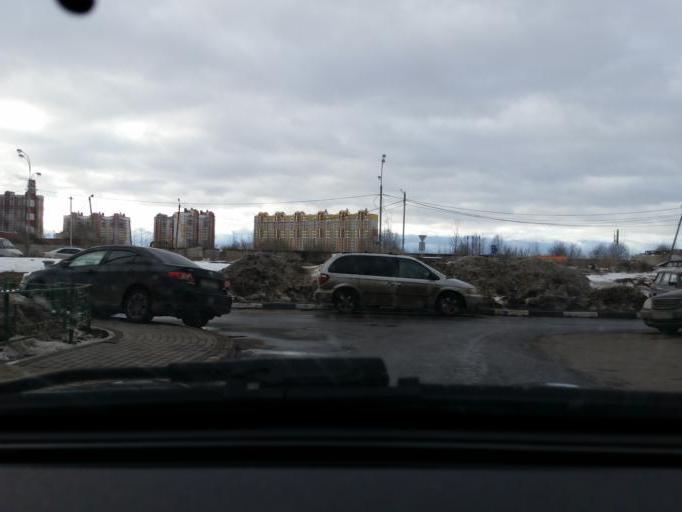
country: RU
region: Moskovskaya
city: Shcherbinka
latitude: 55.5275
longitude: 37.5871
